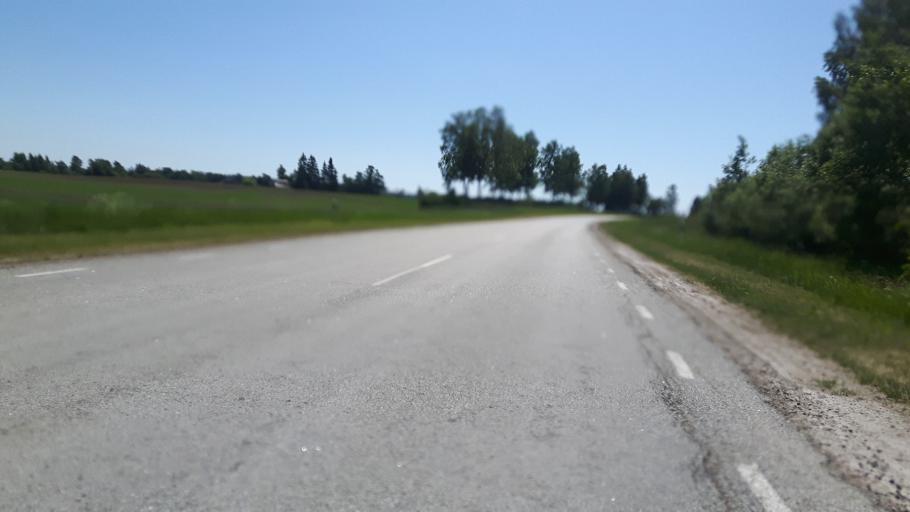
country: EE
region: Paernumaa
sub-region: Sindi linn
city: Sindi
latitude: 58.4305
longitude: 24.7305
